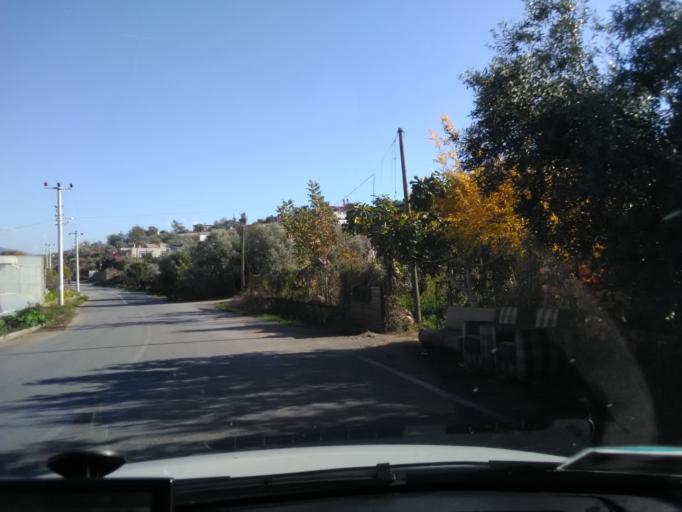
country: TR
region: Antalya
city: Gazipasa
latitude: 36.2589
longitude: 32.3088
